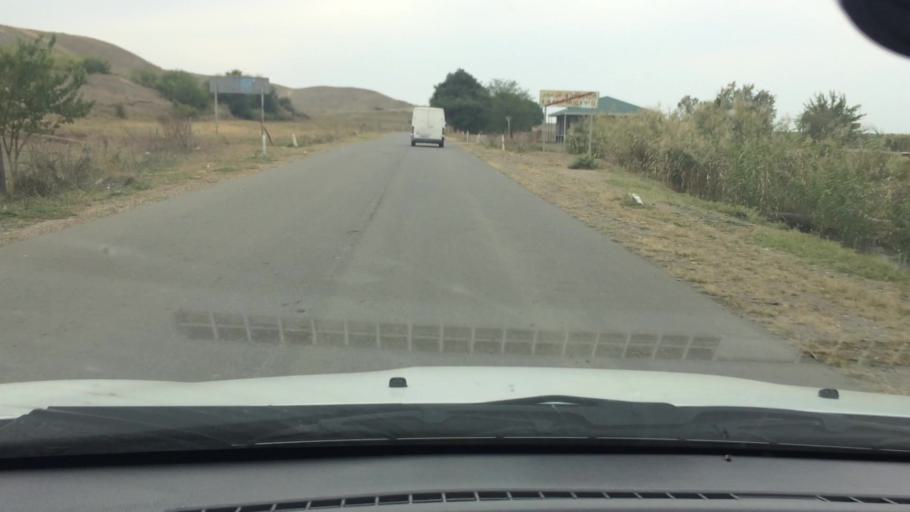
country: AM
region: Tavush
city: Berdavan
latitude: 41.3344
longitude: 45.0331
